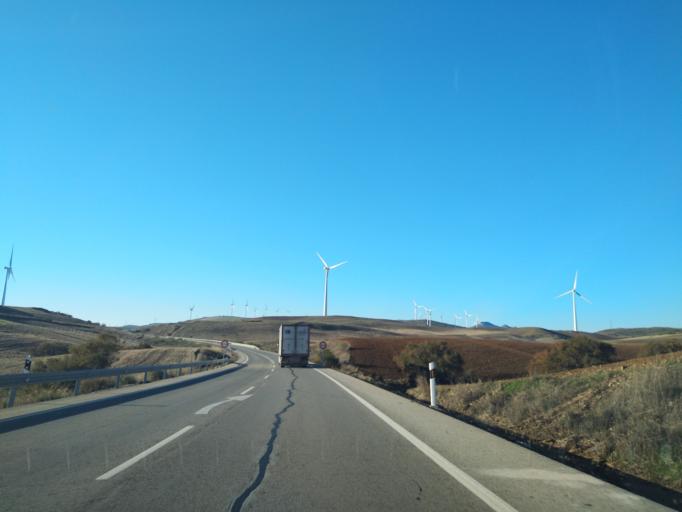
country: ES
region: Andalusia
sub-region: Provincia de Malaga
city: Teba
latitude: 36.9495
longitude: -4.8648
